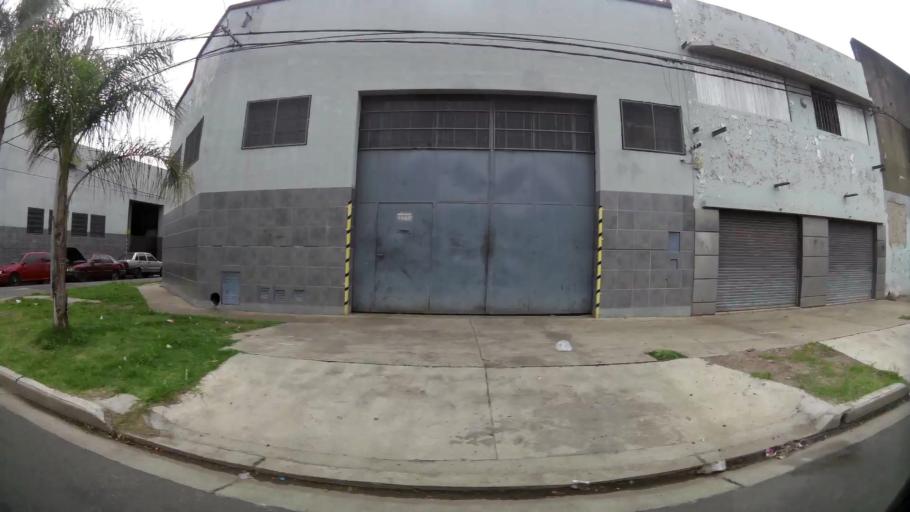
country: AR
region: Santa Fe
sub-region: Departamento de Rosario
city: Rosario
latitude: -32.9860
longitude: -60.6549
